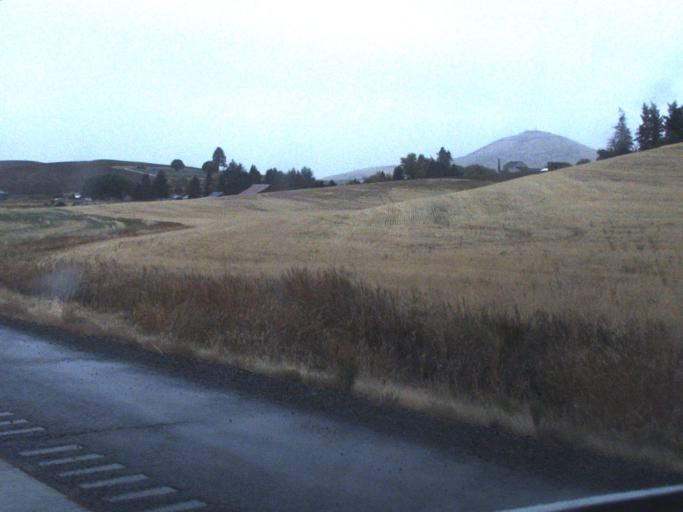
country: US
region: Washington
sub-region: Whitman County
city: Colfax
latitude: 46.9984
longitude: -117.3540
